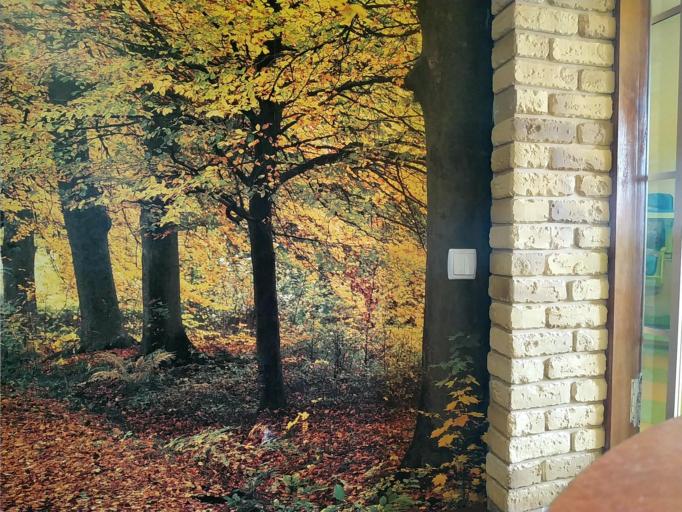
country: RU
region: Smolensk
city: Katyn'
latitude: 54.9170
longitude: 31.7615
